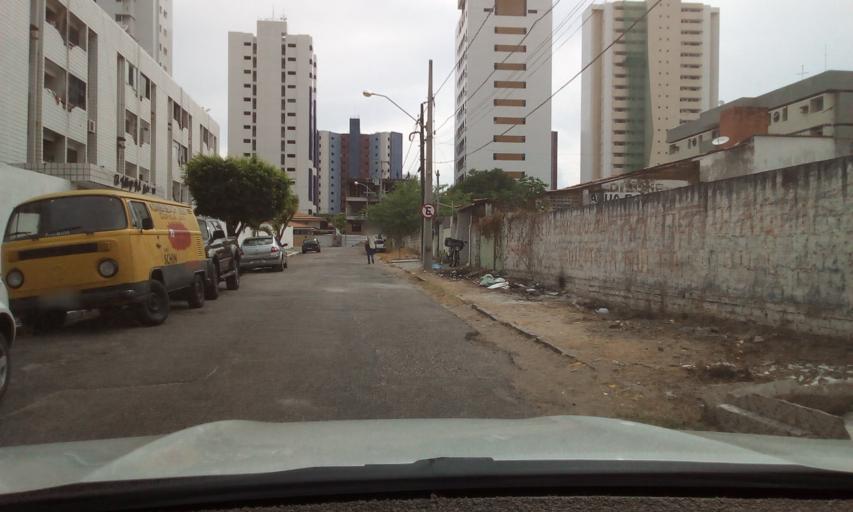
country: BR
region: Paraiba
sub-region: Joao Pessoa
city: Joao Pessoa
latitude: -7.0960
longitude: -34.8453
